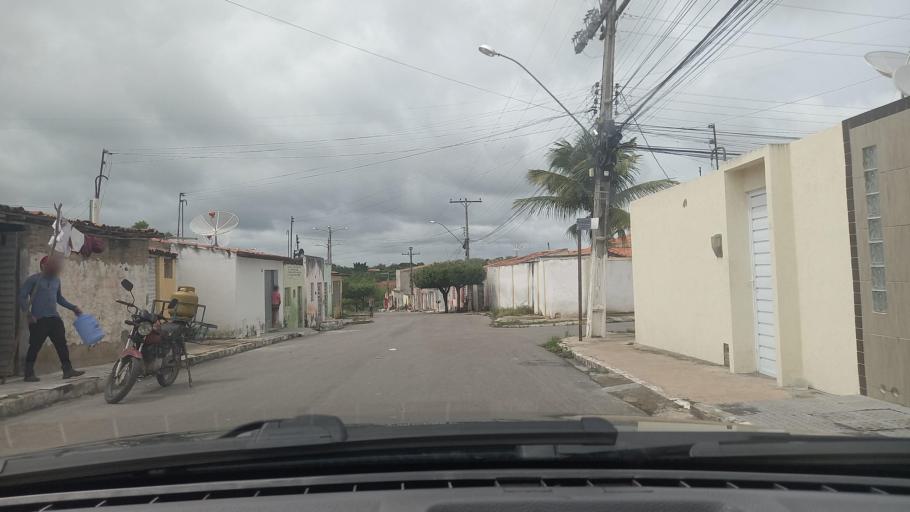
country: BR
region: Alagoas
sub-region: Delmiro Gouveia
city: Delmiro Gouveia
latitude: -9.3916
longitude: -37.9971
